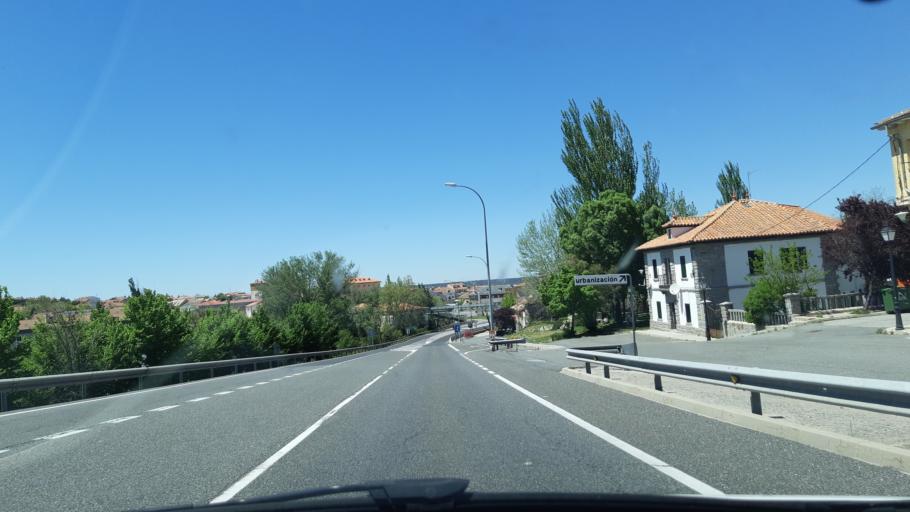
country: ES
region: Castille and Leon
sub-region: Provincia de Segovia
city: Villacastin
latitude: 40.7783
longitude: -4.4066
